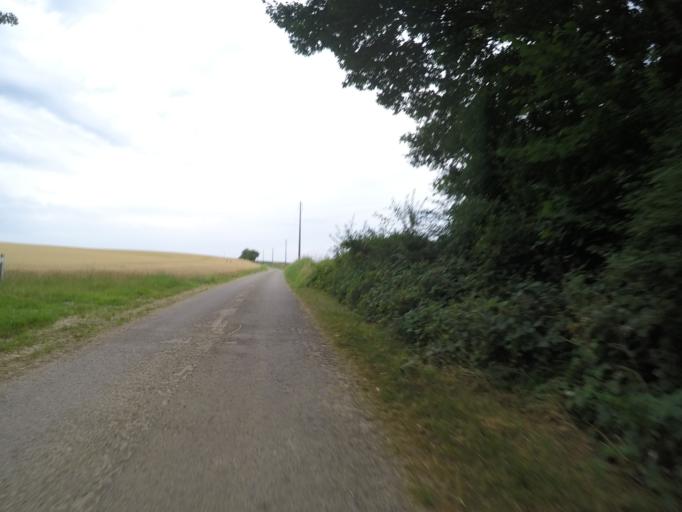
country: BE
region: Wallonia
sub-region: Province de Namur
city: Assesse
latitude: 50.3141
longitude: 5.0063
